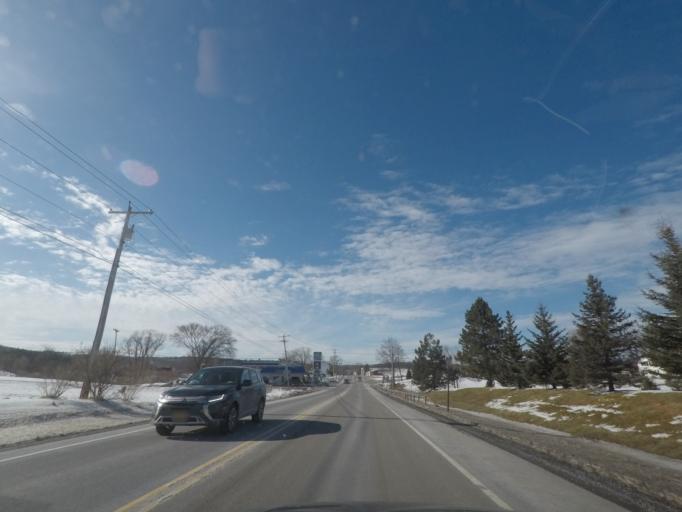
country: US
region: New York
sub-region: Albany County
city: Altamont
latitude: 42.7500
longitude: -74.0466
